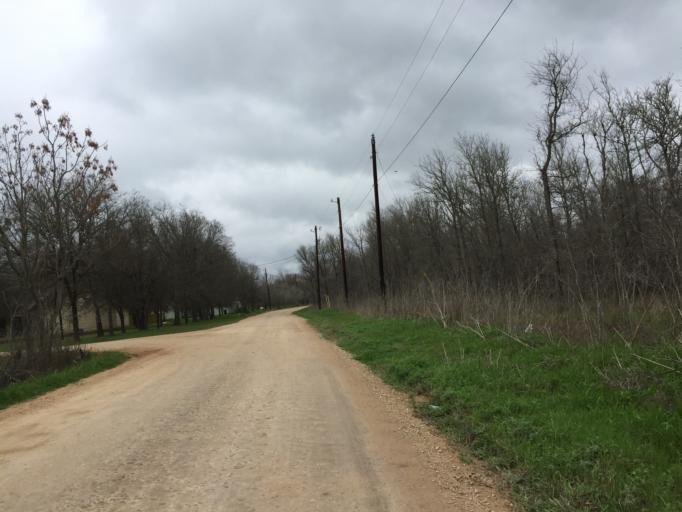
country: US
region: Texas
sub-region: Bastrop County
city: Bastrop
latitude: 30.0887
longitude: -97.3186
